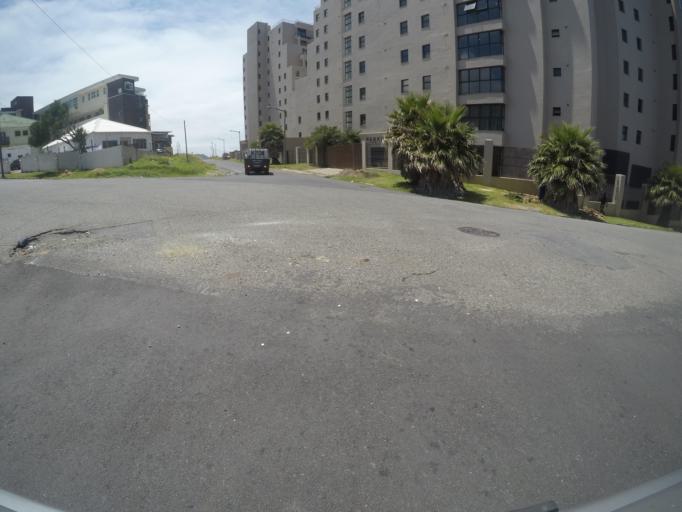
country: ZA
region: Eastern Cape
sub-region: Buffalo City Metropolitan Municipality
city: East London
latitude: -33.0185
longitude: 27.9176
